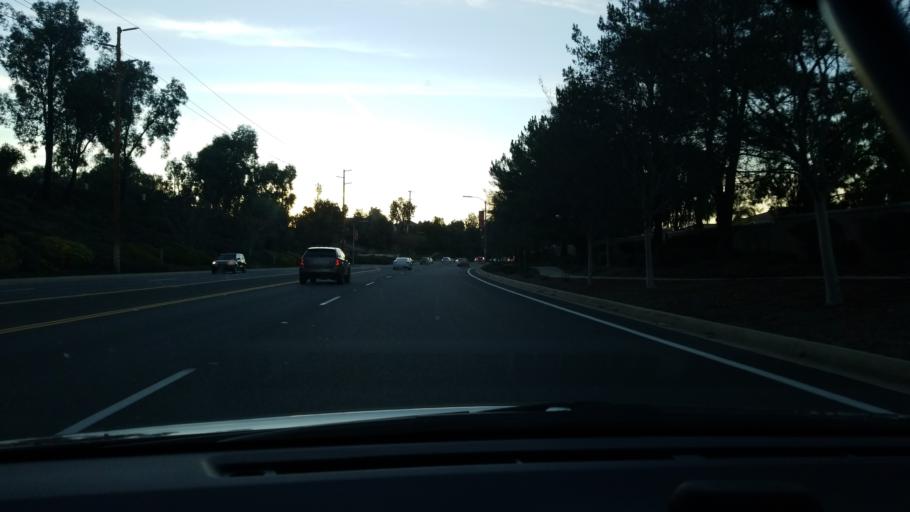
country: US
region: California
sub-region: Riverside County
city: Temecula
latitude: 33.5079
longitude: -117.1181
